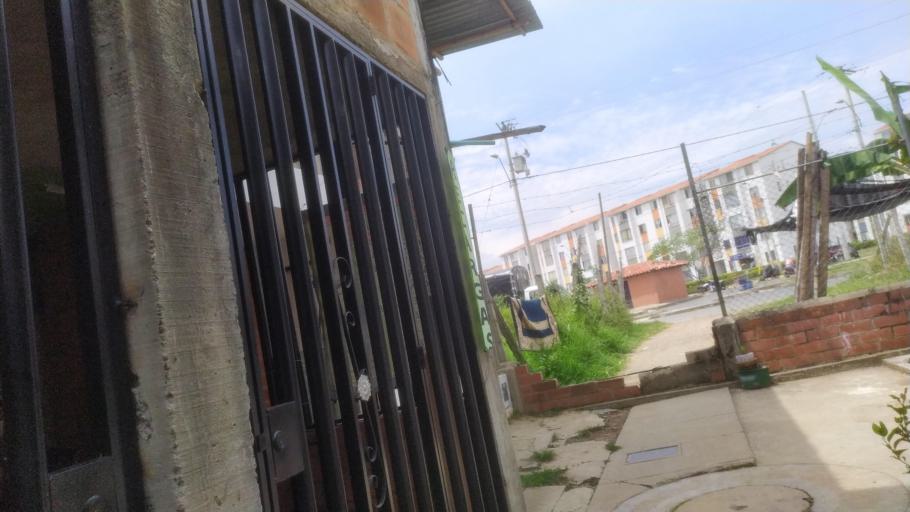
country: CO
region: Valle del Cauca
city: Jamundi
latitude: 3.2360
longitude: -76.5077
